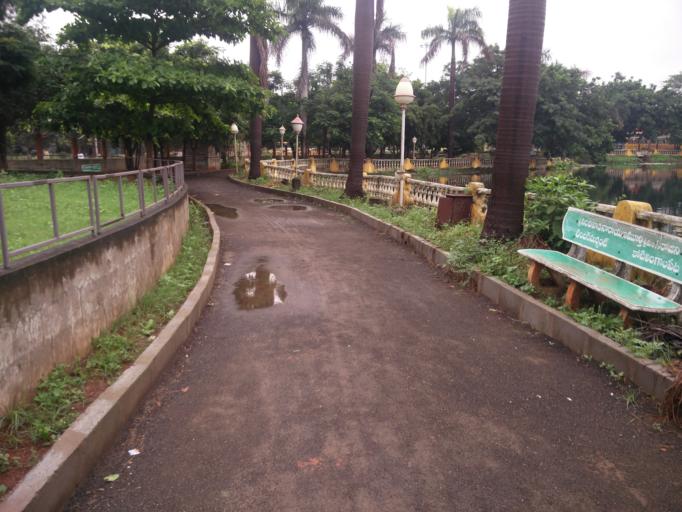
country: IN
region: Andhra Pradesh
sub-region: East Godavari
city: Rajahmundry
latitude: 17.0134
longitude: 81.7786
